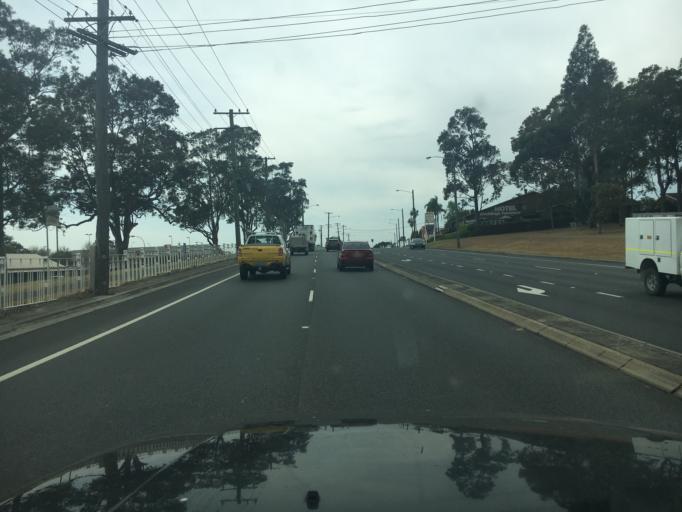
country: AU
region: New South Wales
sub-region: Maitland Municipality
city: Rutherford
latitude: -32.7157
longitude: 151.5255
